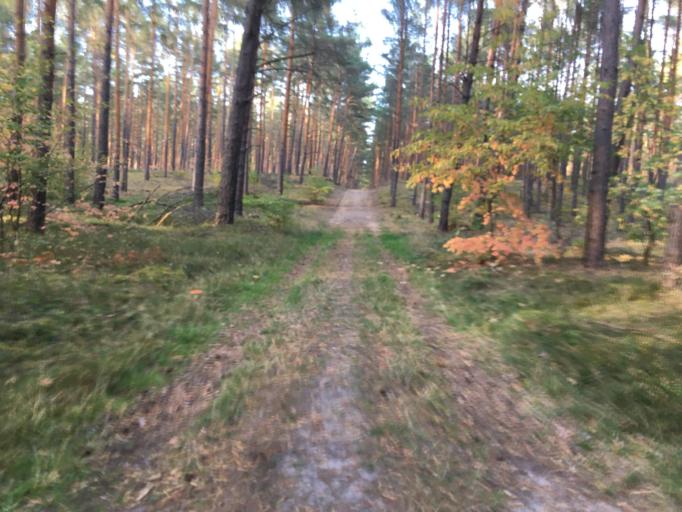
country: DE
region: Brandenburg
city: Birkenwerder
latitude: 52.6974
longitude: 13.3316
